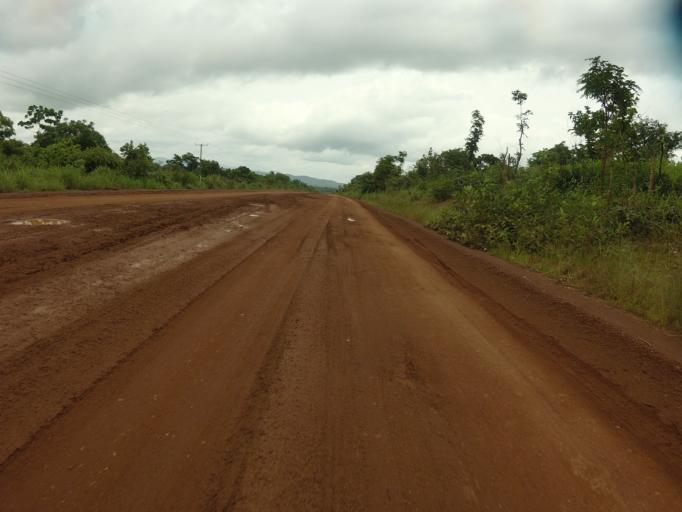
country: GH
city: Kpandae
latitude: 8.3054
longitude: 0.4849
